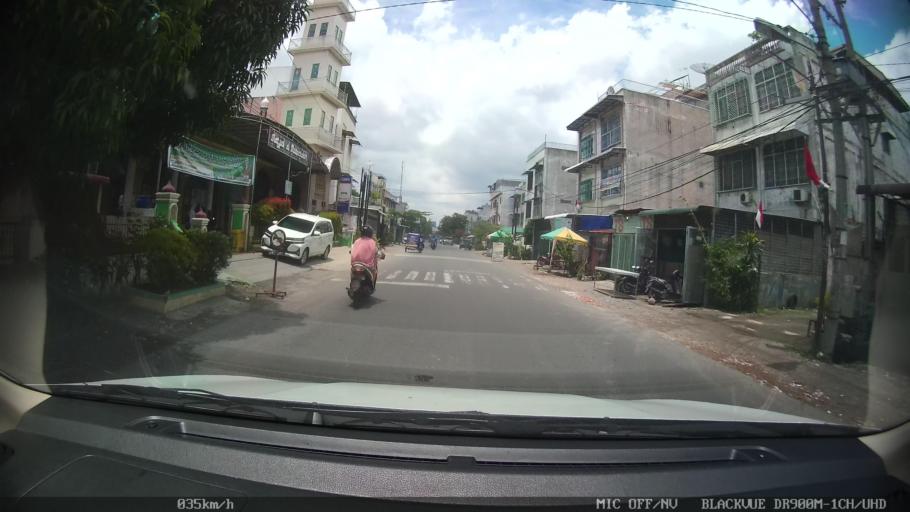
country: ID
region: North Sumatra
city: Medan
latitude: 3.5947
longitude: 98.7095
